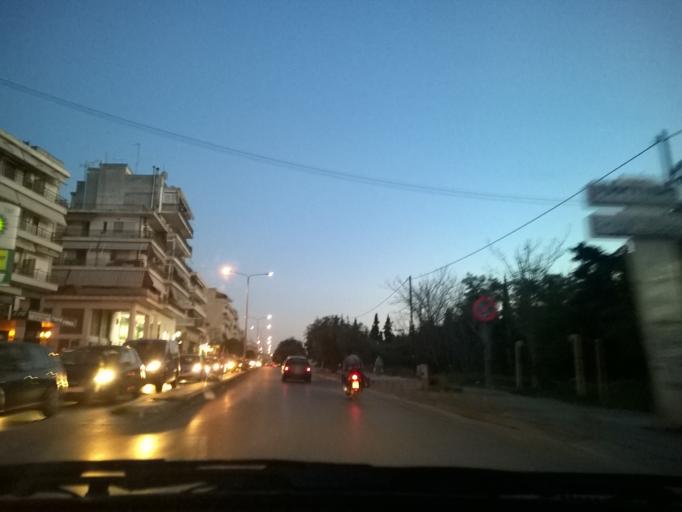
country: GR
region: Central Macedonia
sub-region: Nomos Thessalonikis
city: Ampelokipoi
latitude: 40.6560
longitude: 22.9344
